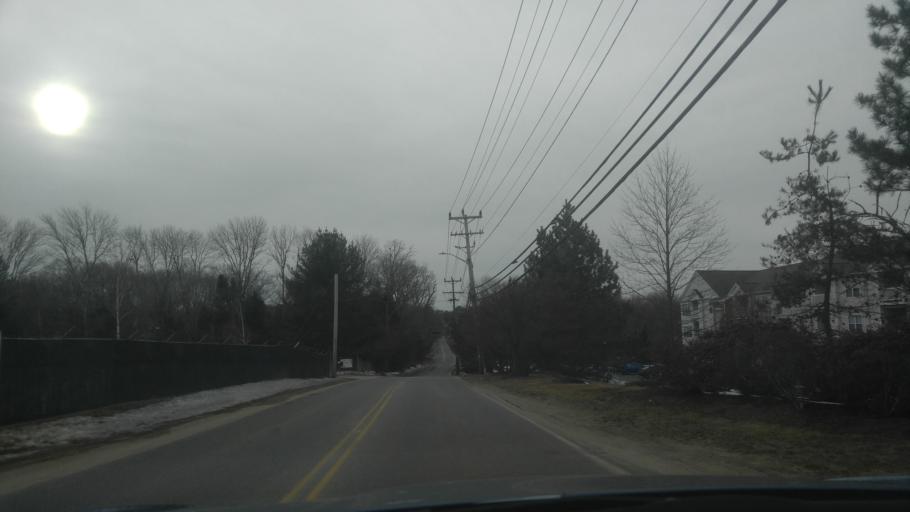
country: US
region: Rhode Island
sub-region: Kent County
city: West Warwick
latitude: 41.6737
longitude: -71.5024
